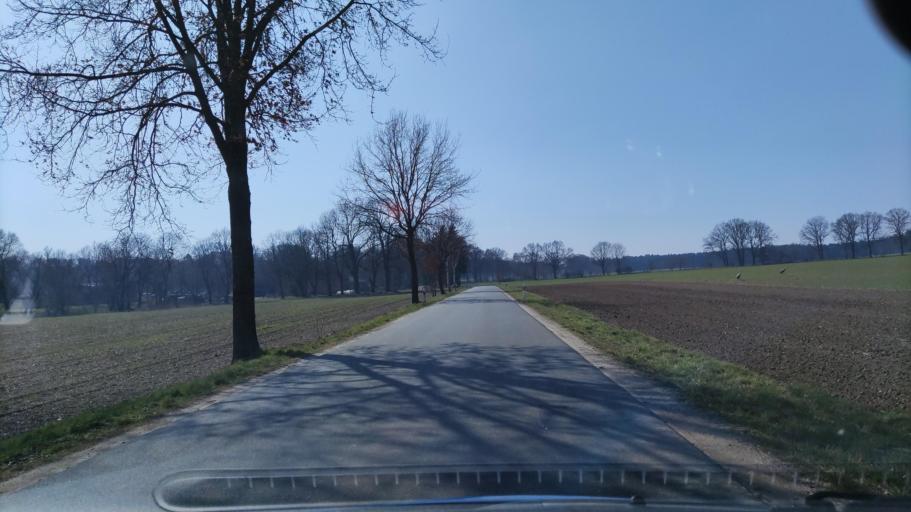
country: DE
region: Lower Saxony
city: Zernien
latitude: 52.9872
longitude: 10.8740
